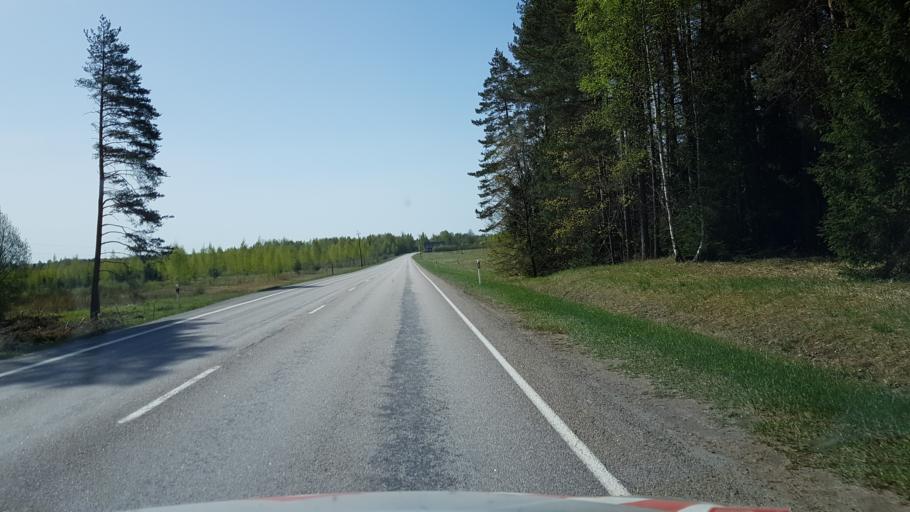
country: EE
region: Valgamaa
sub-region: Valga linn
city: Valga
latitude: 57.8136
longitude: 26.0425
